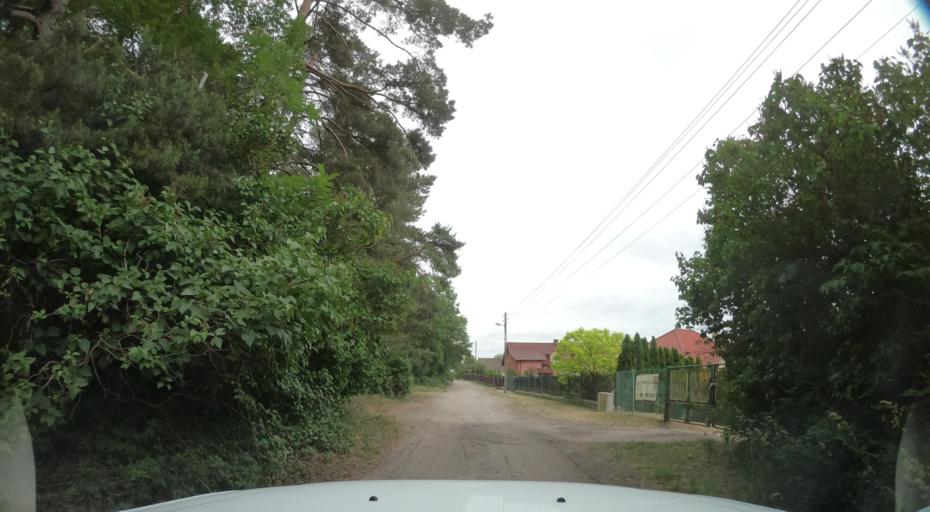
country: PL
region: West Pomeranian Voivodeship
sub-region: Powiat kamienski
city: Miedzyzdroje
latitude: 53.8604
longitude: 14.5180
